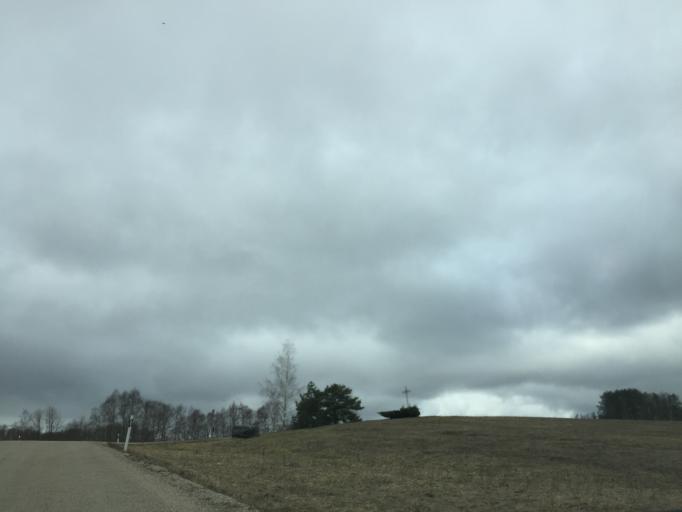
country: LV
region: Ilukste
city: Ilukste
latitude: 56.0425
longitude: 26.1979
